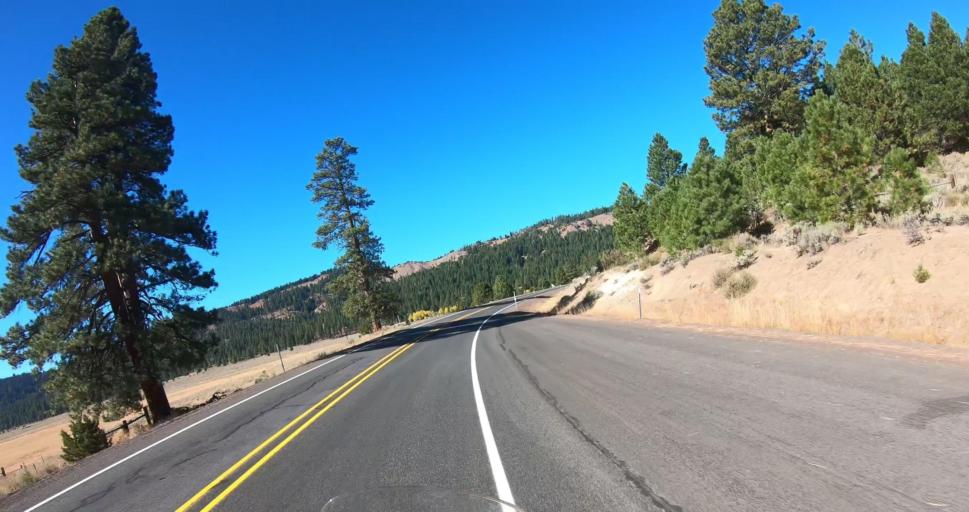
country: US
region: Oregon
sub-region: Lake County
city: Lakeview
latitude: 42.2287
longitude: -120.2777
